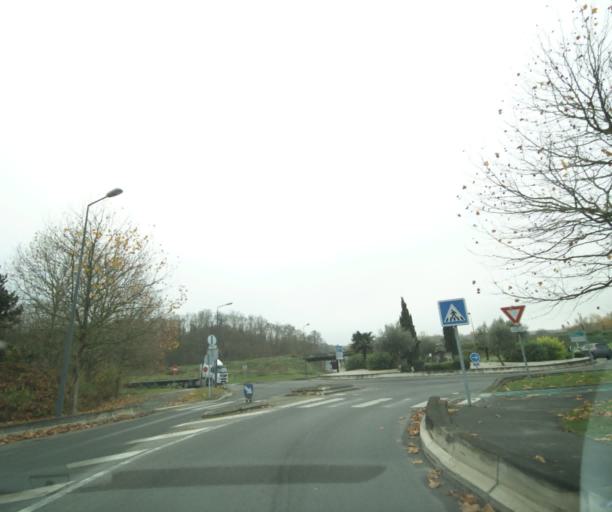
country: FR
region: Ile-de-France
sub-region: Departement de Seine-et-Marne
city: Villeparisis
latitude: 48.9356
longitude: 2.6020
